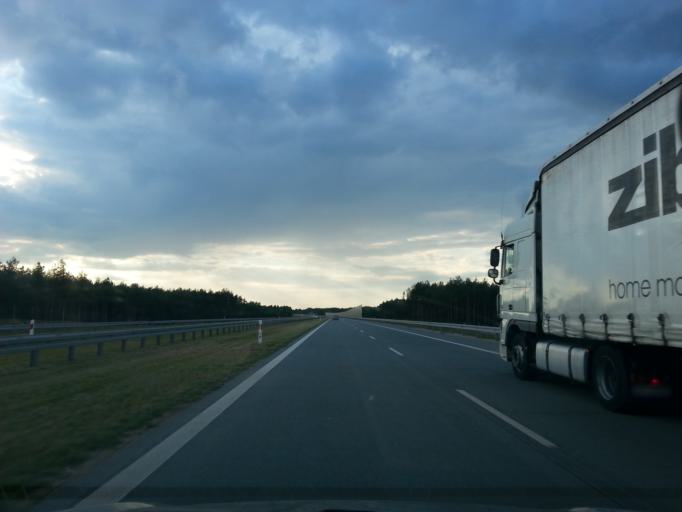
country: PL
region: Lodz Voivodeship
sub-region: Powiat zdunskowolski
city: Zdunska Wola
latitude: 51.5866
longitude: 18.8975
